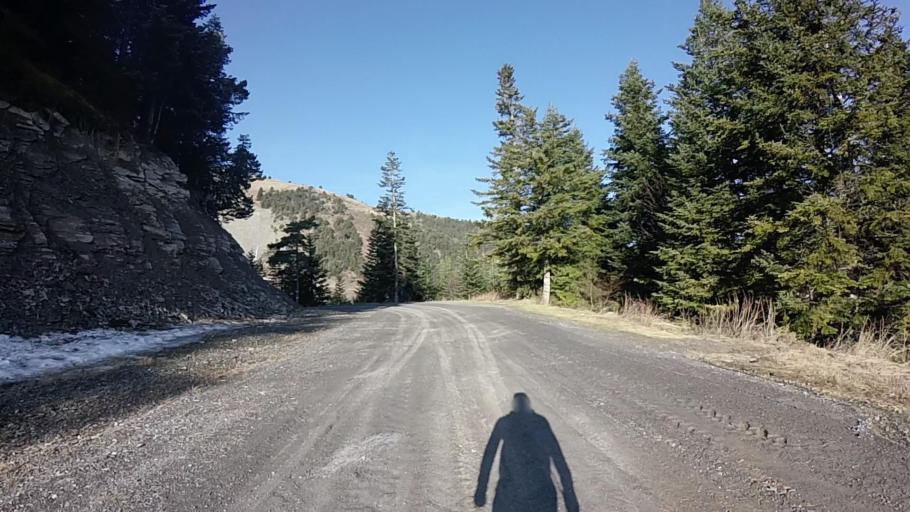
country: FR
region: Provence-Alpes-Cote d'Azur
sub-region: Departement des Alpes-de-Haute-Provence
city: Seyne-les-Alpes
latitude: 44.3462
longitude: 6.2914
